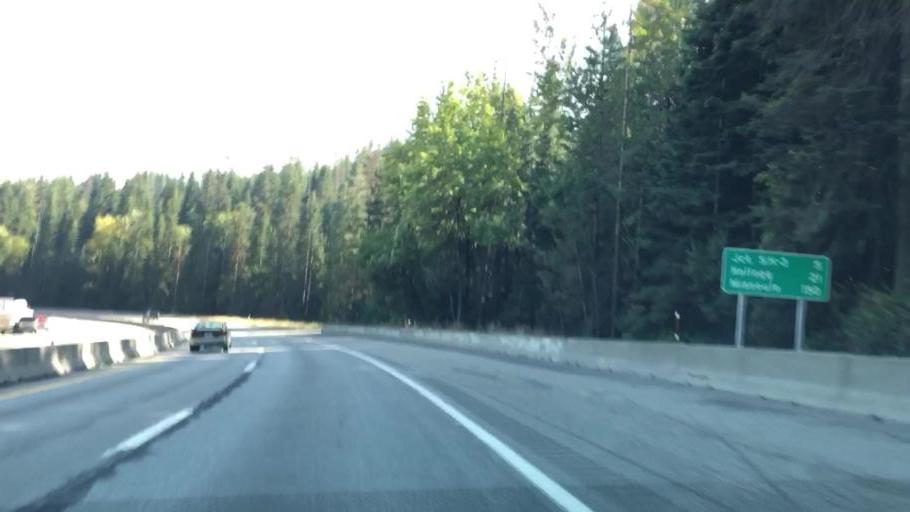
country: US
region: Idaho
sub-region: Kootenai County
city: Coeur d'Alene
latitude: 47.6127
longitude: -116.5211
